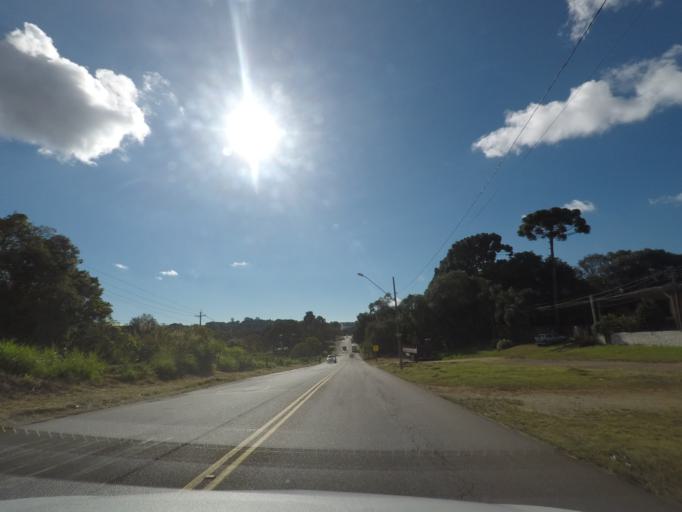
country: BR
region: Parana
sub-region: Almirante Tamandare
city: Almirante Tamandare
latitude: -25.3660
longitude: -49.2770
